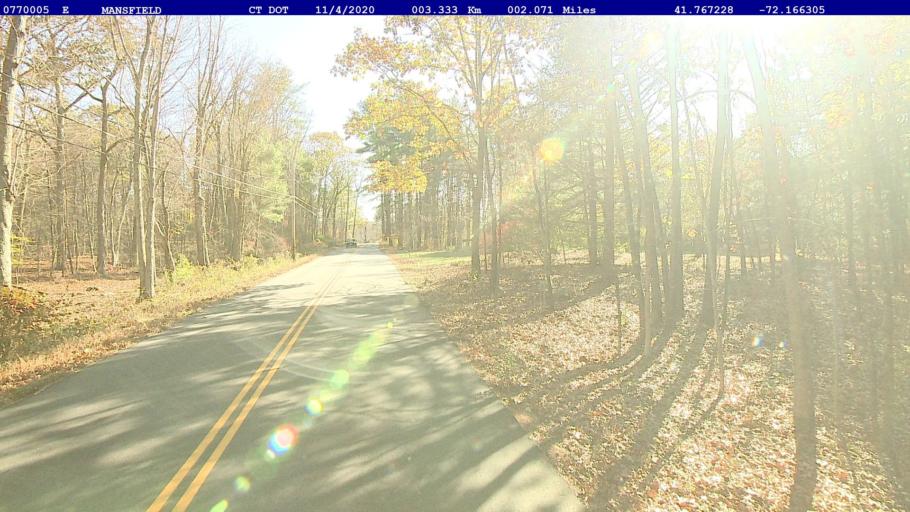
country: US
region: Connecticut
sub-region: Tolland County
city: Mansfield City
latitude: 41.7672
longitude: -72.1663
